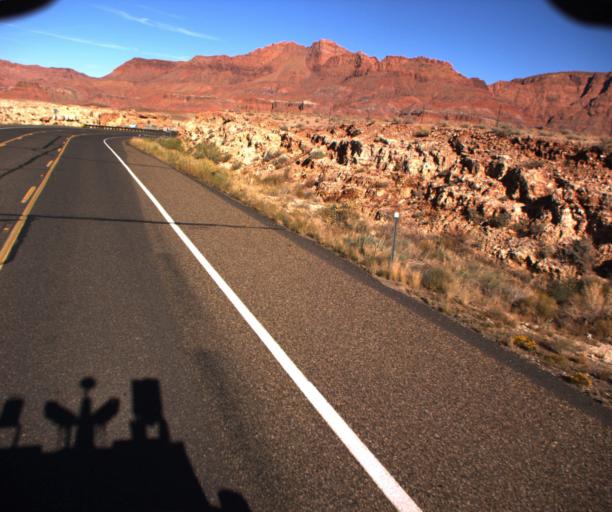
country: US
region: Arizona
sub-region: Coconino County
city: Page
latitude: 36.8171
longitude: -111.6358
